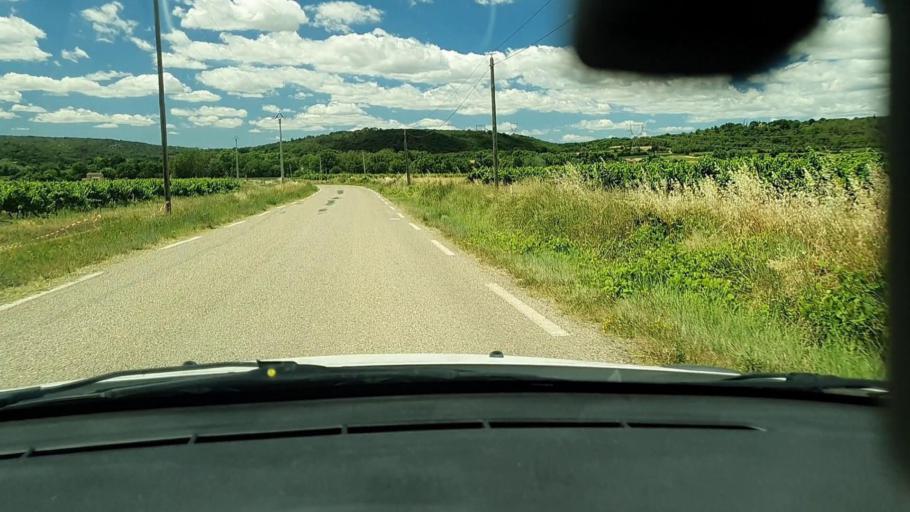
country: FR
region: Languedoc-Roussillon
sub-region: Departement du Gard
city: Blauzac
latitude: 43.9502
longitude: 4.3914
